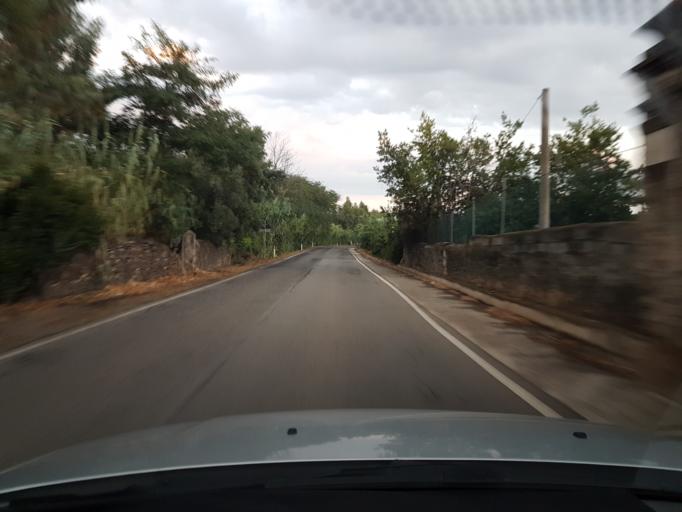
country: IT
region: Sardinia
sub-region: Provincia di Oristano
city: Milis
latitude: 40.0422
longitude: 8.6354
